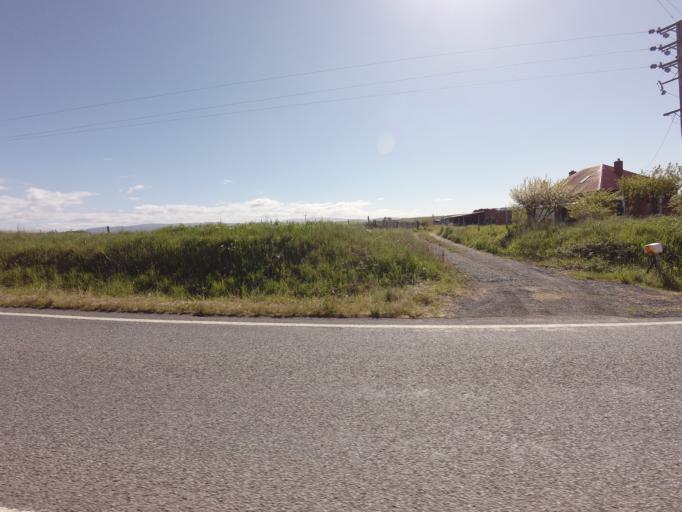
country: AU
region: Tasmania
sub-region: Derwent Valley
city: New Norfolk
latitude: -42.6913
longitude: 146.9413
